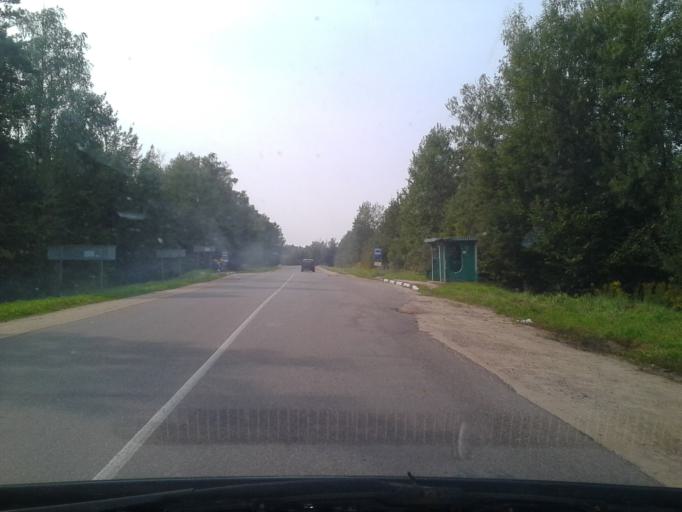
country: BY
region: Minsk
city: Hatava
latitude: 53.7717
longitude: 27.6590
